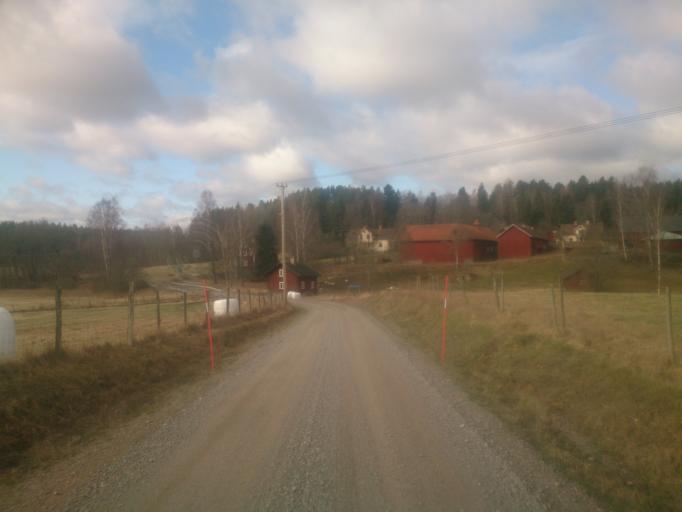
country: SE
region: OEstergoetland
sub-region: Atvidabergs Kommun
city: Atvidaberg
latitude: 58.2113
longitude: 16.1685
